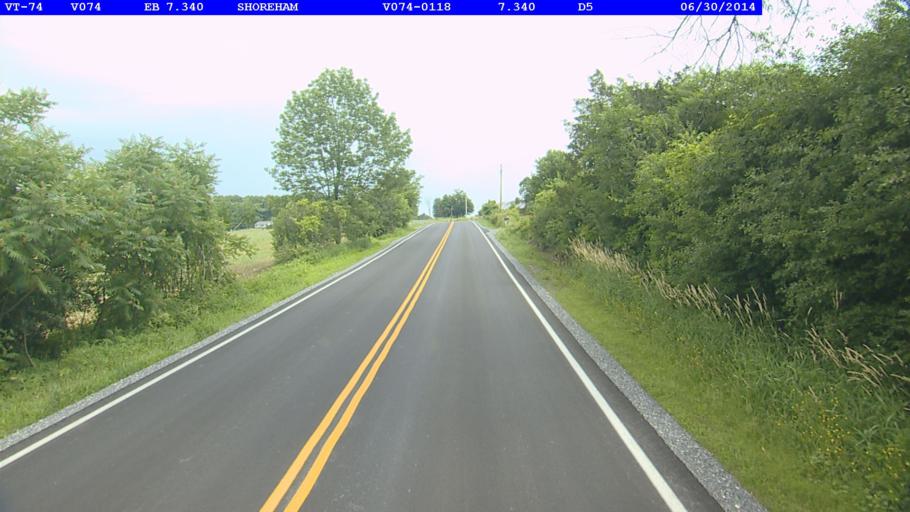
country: US
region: New York
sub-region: Essex County
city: Ticonderoga
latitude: 43.9247
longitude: -73.2918
